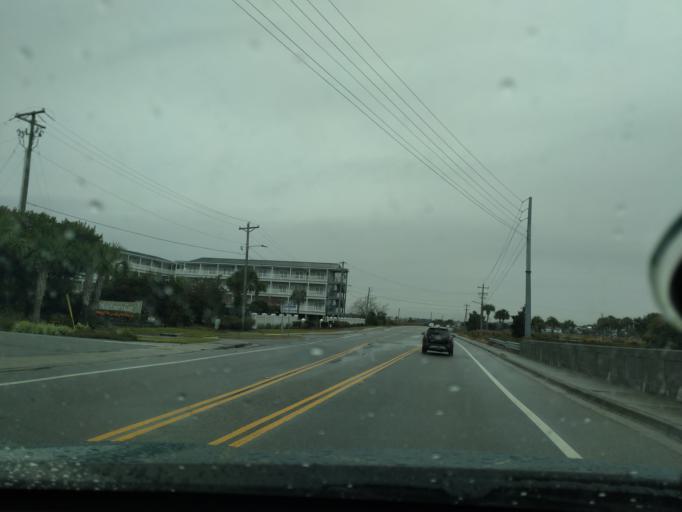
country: US
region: South Carolina
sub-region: Charleston County
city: Folly Beach
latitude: 32.6630
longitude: -79.9441
